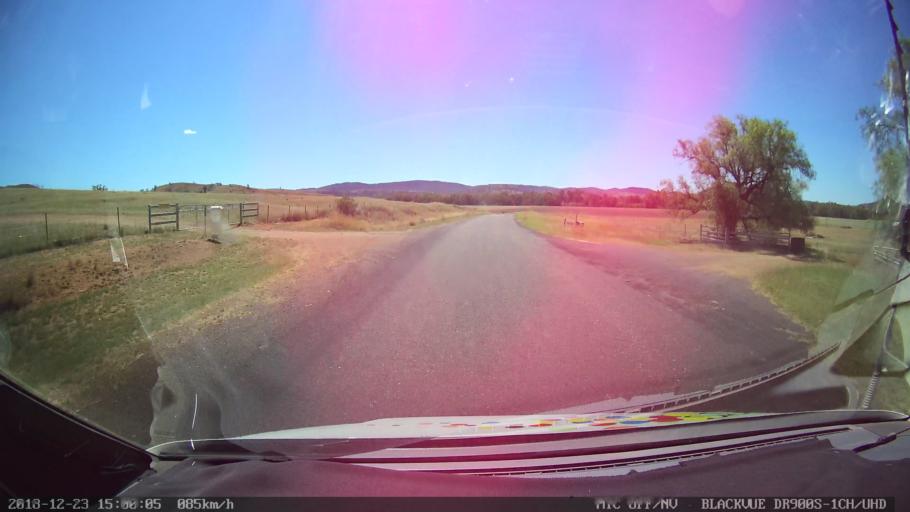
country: AU
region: New South Wales
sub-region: Tamworth Municipality
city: Manilla
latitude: -30.7233
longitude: 150.7918
